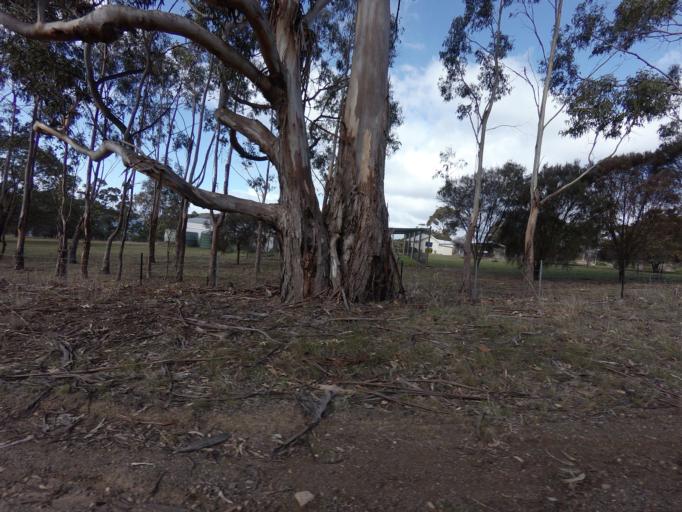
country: AU
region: Tasmania
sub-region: Sorell
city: Sorell
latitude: -42.3274
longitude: 147.9682
